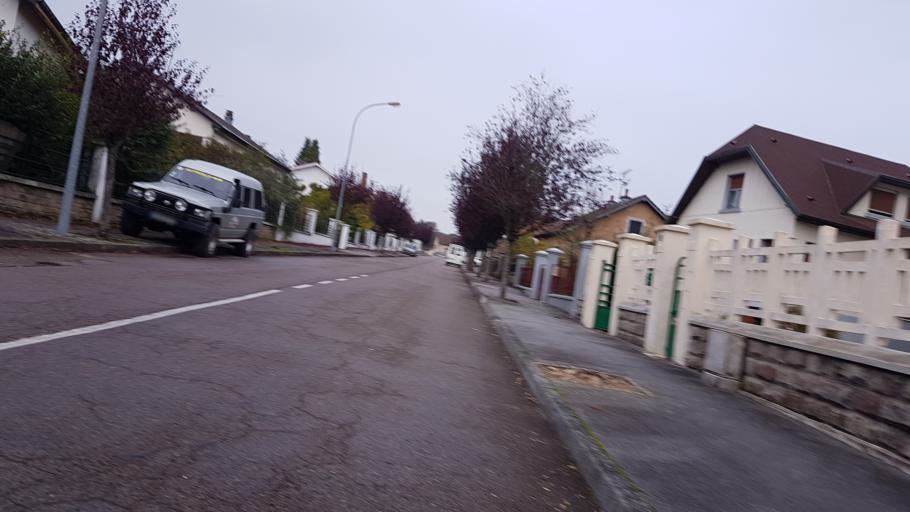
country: FR
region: Franche-Comte
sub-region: Departement de la Haute-Saone
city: Luxeuil-les-Bains
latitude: 47.8219
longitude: 6.3720
